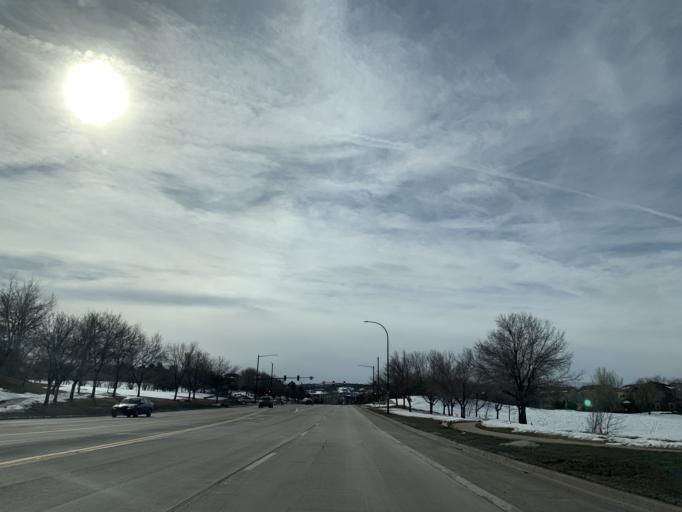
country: US
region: Colorado
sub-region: Douglas County
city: Carriage Club
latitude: 39.5271
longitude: -104.9168
